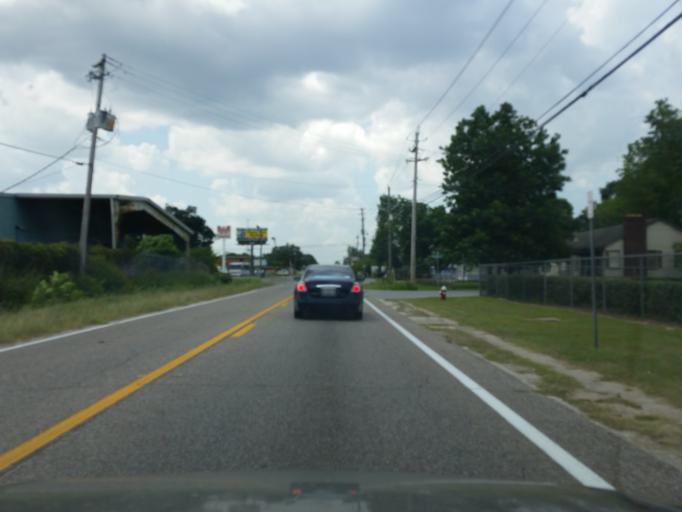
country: US
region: Florida
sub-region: Escambia County
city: Brent
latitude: 30.4704
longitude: -87.2436
